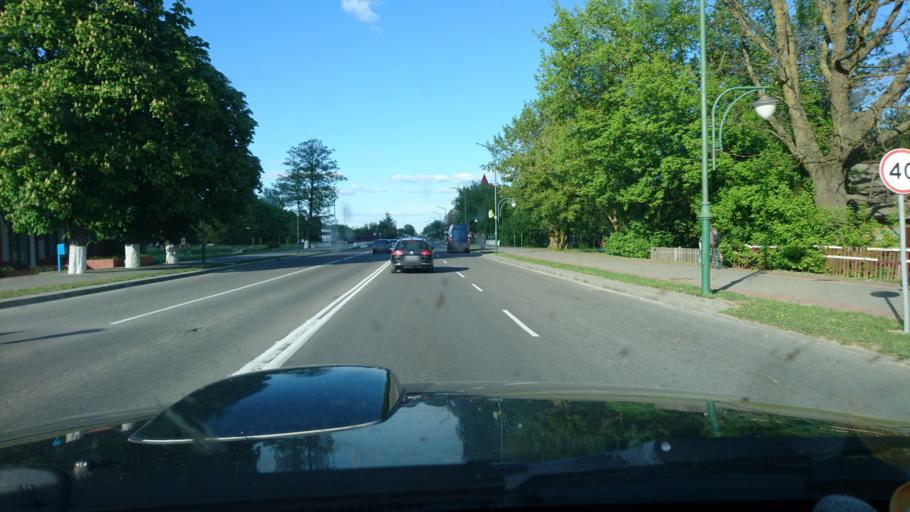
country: BY
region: Brest
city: Byaroza
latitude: 52.5357
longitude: 24.9875
